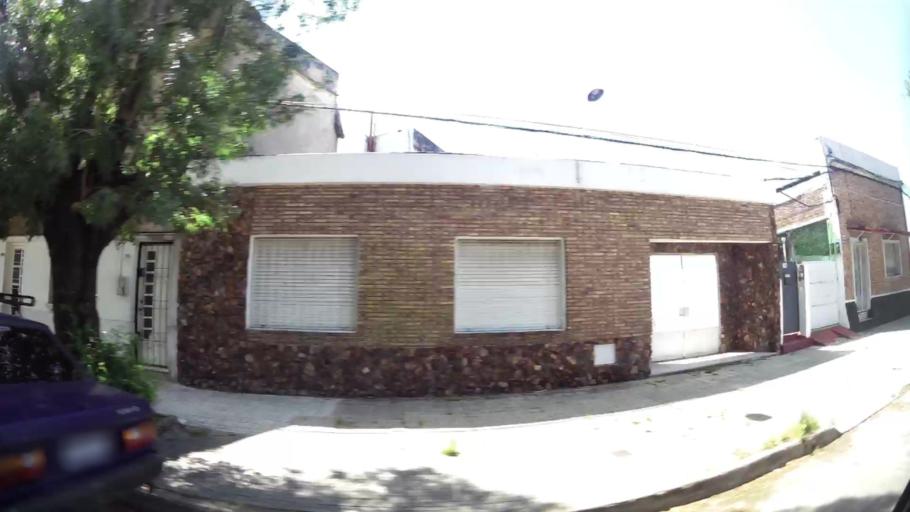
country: UY
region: Montevideo
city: Montevideo
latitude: -34.8675
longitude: -56.1776
